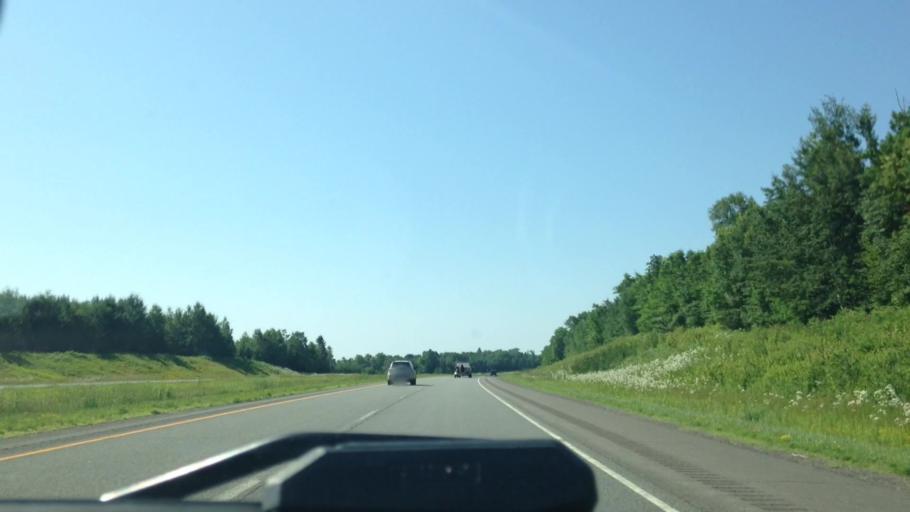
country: US
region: Wisconsin
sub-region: Douglas County
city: Lake Nebagamon
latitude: 46.4243
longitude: -91.8105
